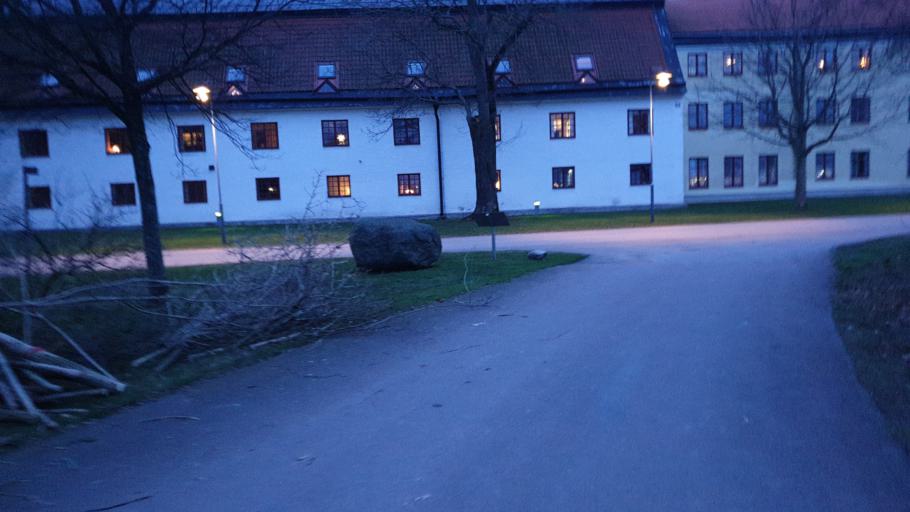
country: SE
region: Blekinge
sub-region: Karlskrona Kommun
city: Karlskrona
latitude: 56.1595
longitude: 15.5985
